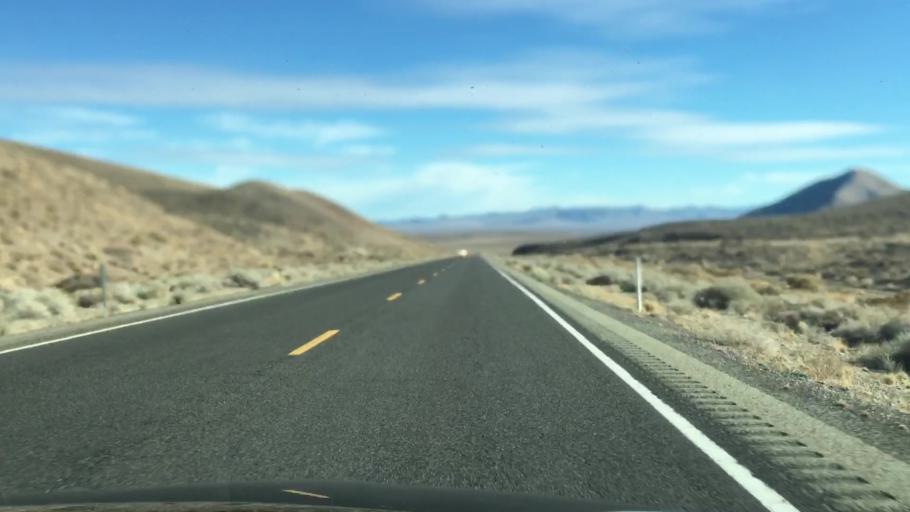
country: US
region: Nevada
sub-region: Lyon County
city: Yerington
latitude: 39.0390
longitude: -118.9354
